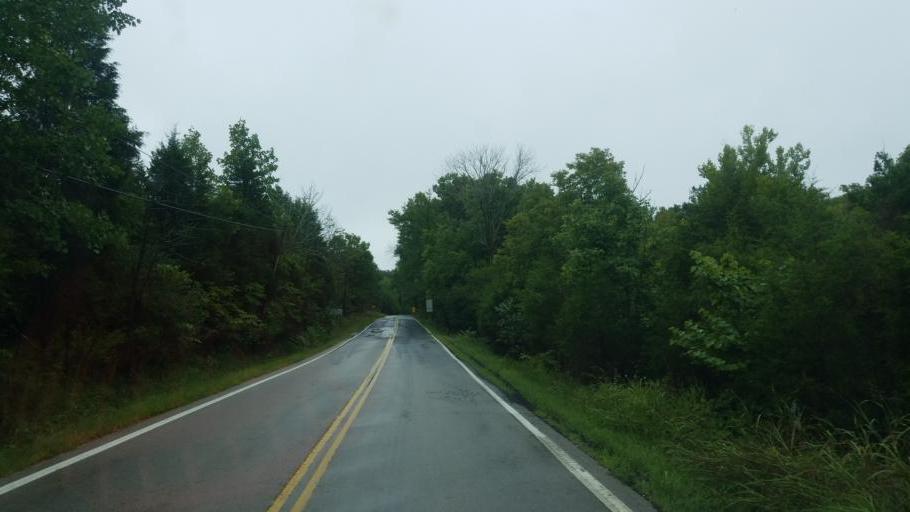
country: US
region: Ohio
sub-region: Adams County
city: West Union
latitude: 38.7886
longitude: -83.5422
